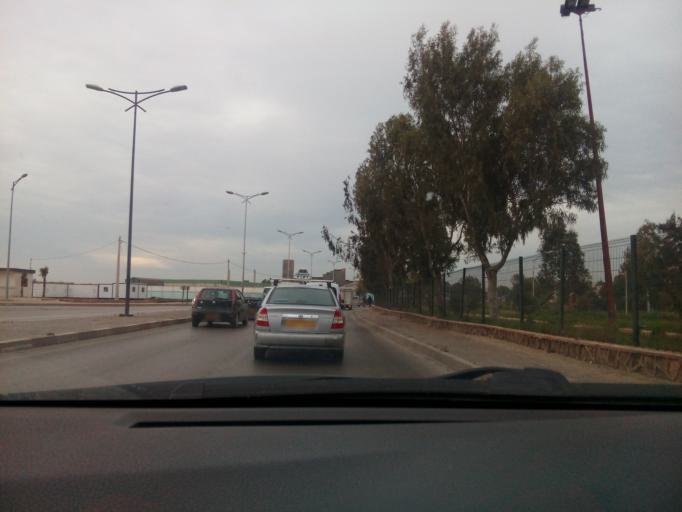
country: DZ
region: Oran
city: Oran
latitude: 35.6780
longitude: -0.6159
